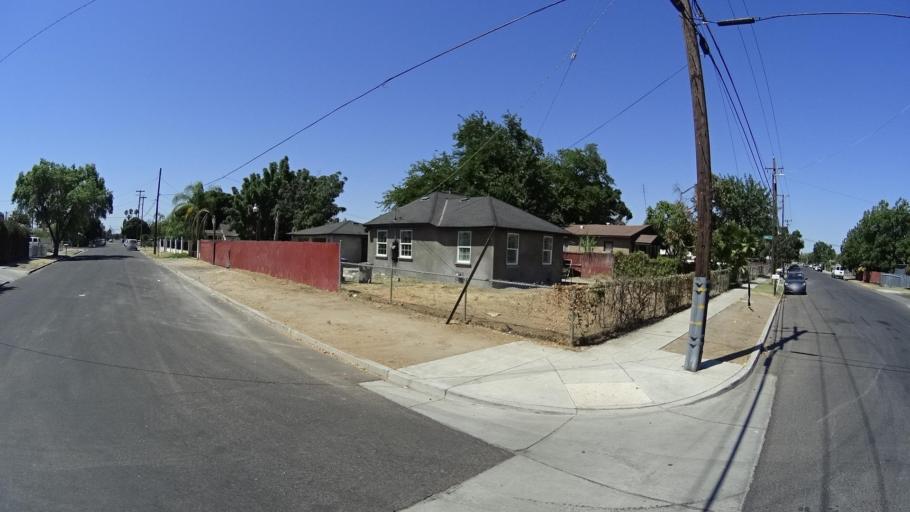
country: US
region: California
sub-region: Fresno County
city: Fresno
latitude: 36.7631
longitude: -119.7522
